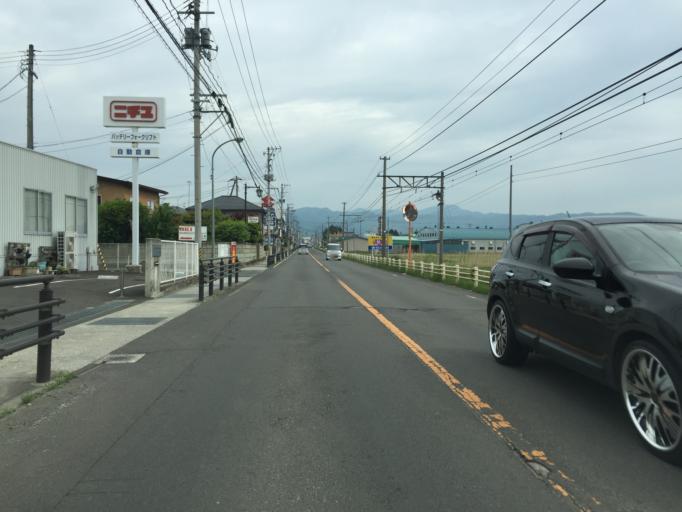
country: JP
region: Fukushima
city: Fukushima-shi
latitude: 37.8021
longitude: 140.4421
